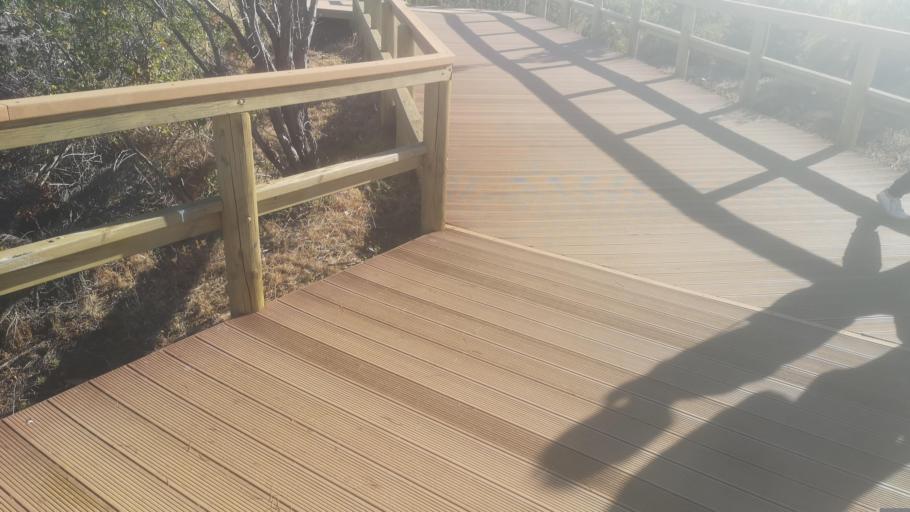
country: AU
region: Western Australia
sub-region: Dandaragan
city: Jurien Bay
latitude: -30.6025
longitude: 115.1615
